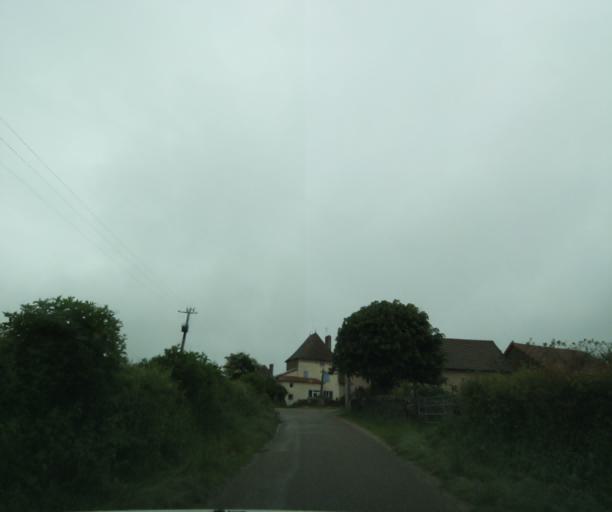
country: FR
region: Bourgogne
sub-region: Departement de Saone-et-Loire
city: Charolles
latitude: 46.3909
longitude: 4.3129
